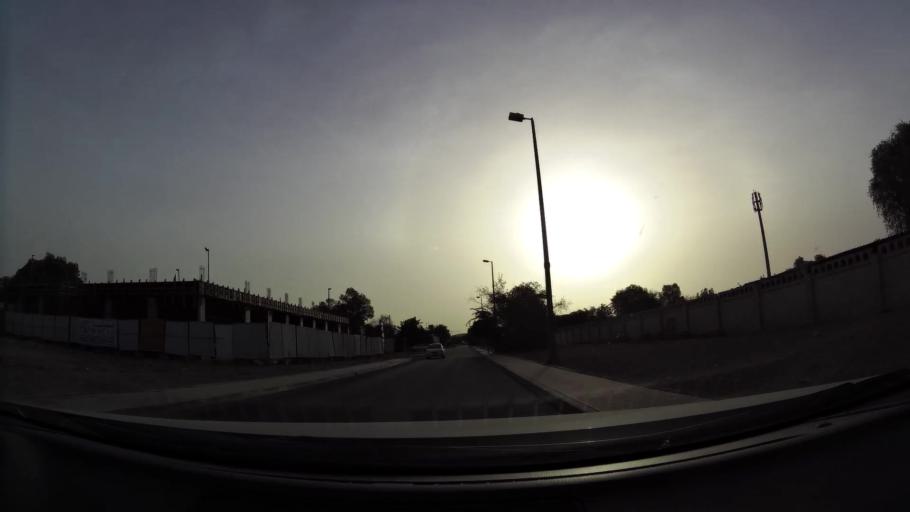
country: OM
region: Al Buraimi
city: Al Buraymi
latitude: 24.2439
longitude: 55.7367
